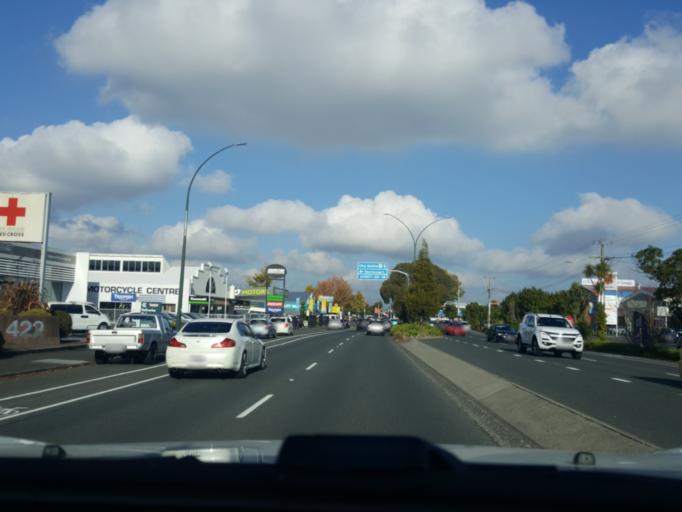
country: NZ
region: Waikato
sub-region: Hamilton City
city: Hamilton
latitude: -37.7630
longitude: 175.2515
